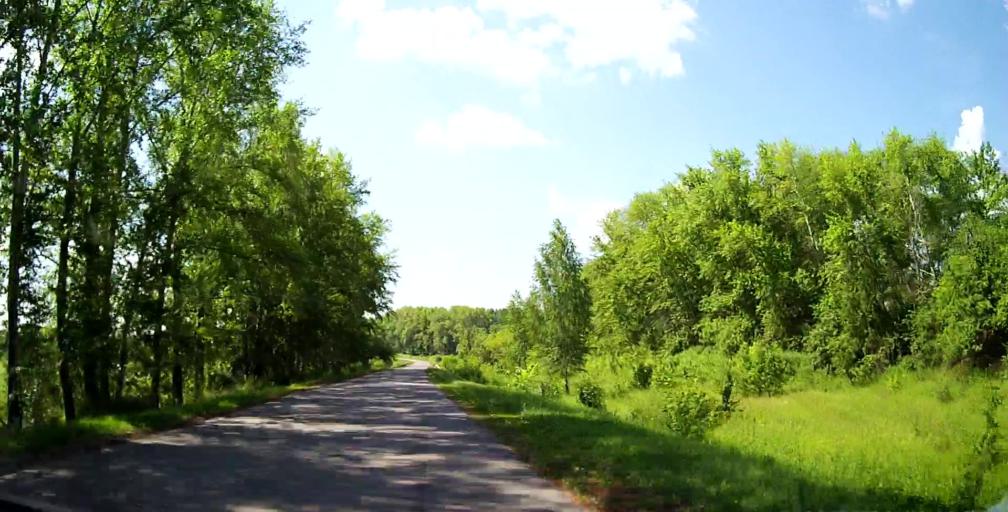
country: RU
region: Lipetsk
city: Chaplygin
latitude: 53.3061
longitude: 39.9528
